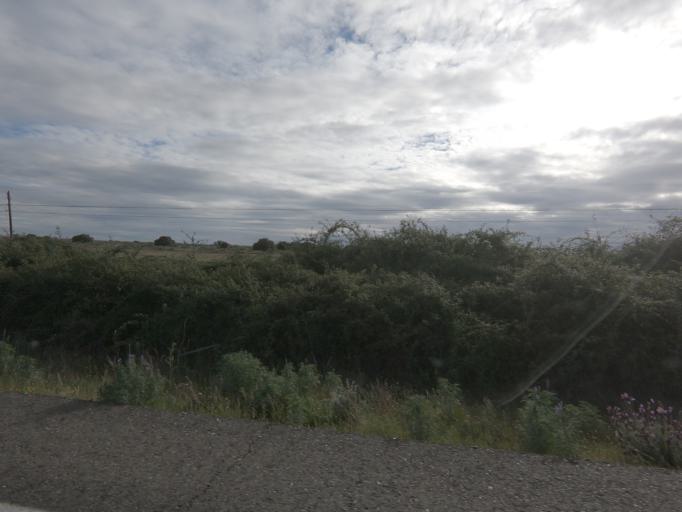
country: ES
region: Extremadura
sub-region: Provincia de Caceres
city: Moraleja
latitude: 40.0533
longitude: -6.6421
